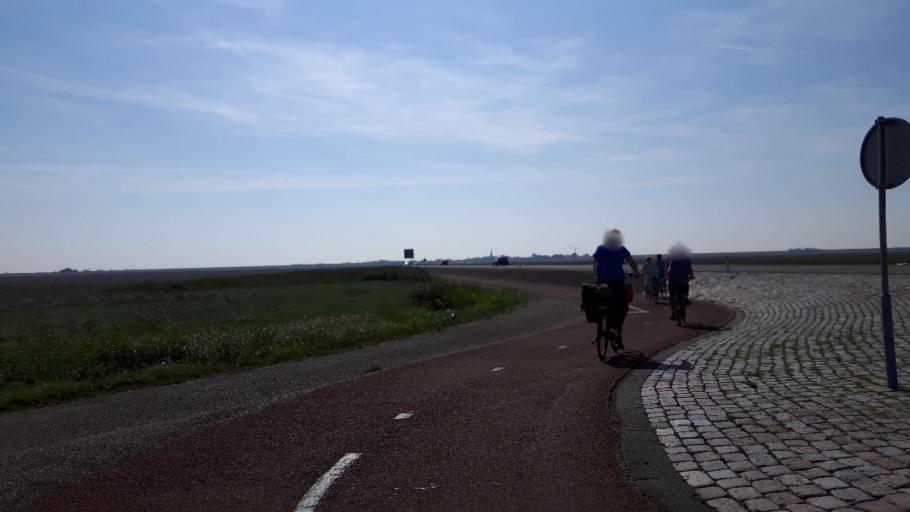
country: NL
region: Friesland
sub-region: Gemeente Dongeradeel
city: Holwerd
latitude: 53.3916
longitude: 5.8831
